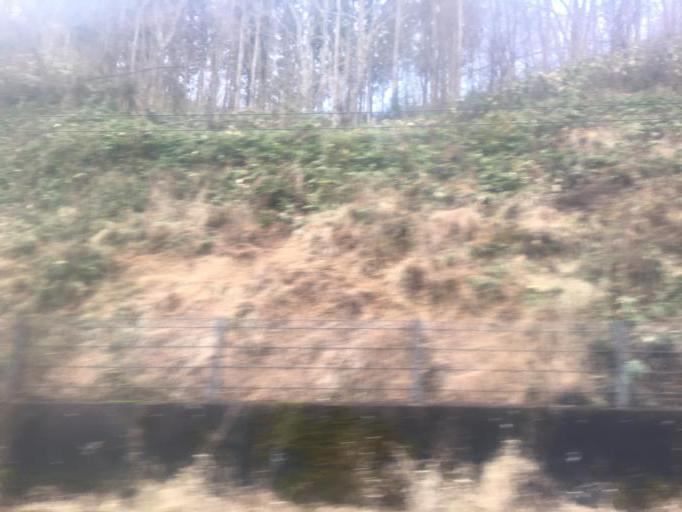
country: JP
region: Akita
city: Takanosu
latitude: 40.2616
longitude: 140.4073
